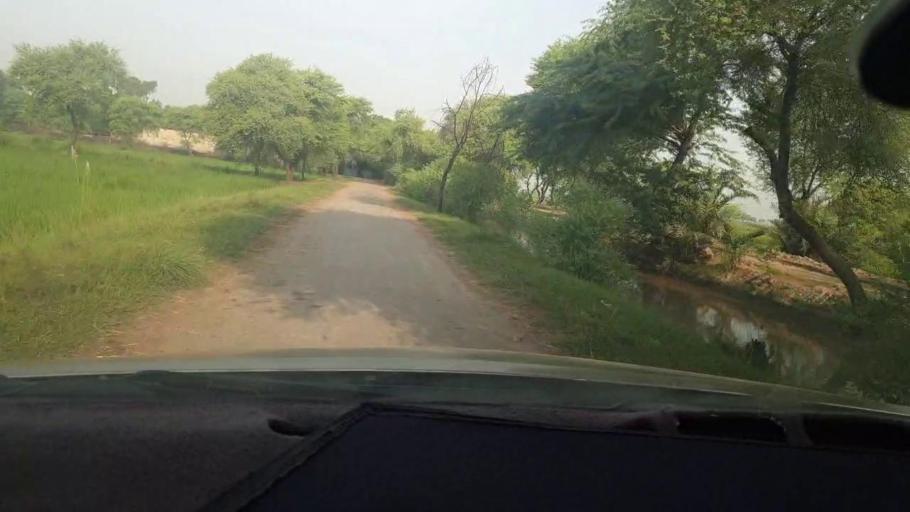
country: PK
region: Sindh
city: Jacobabad
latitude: 28.3091
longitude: 68.4132
